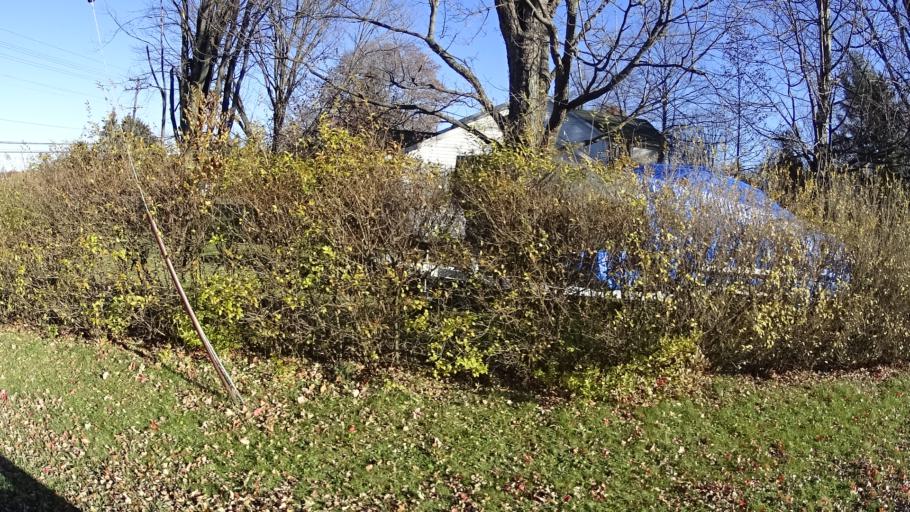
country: US
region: Ohio
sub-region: Lorain County
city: Avon Center
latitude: 41.4528
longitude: -81.9974
